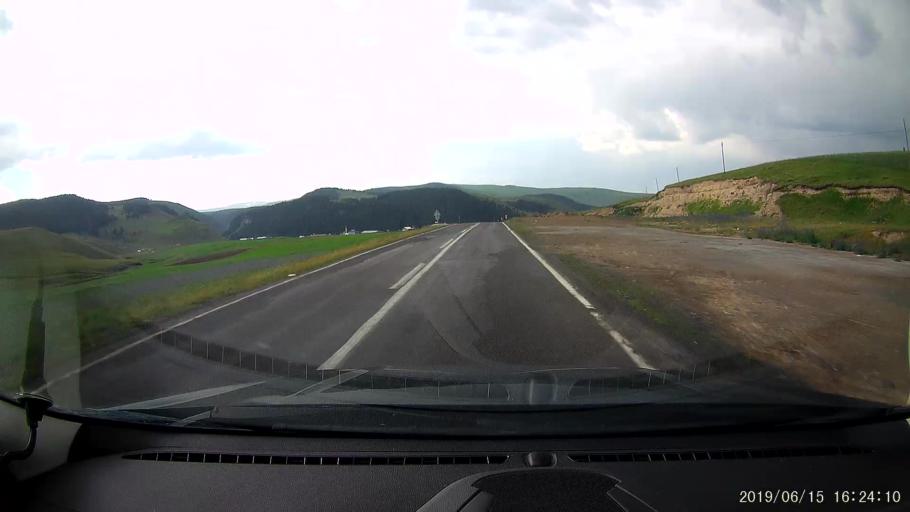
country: TR
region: Ardahan
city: Hanak
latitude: 41.1679
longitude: 42.8687
